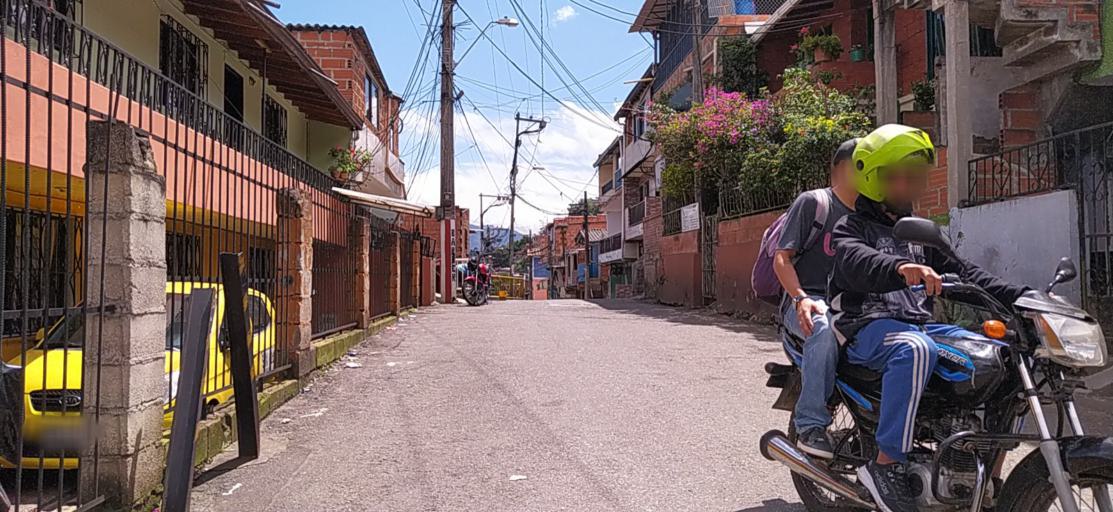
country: CO
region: Antioquia
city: Medellin
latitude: 6.2906
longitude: -75.5420
